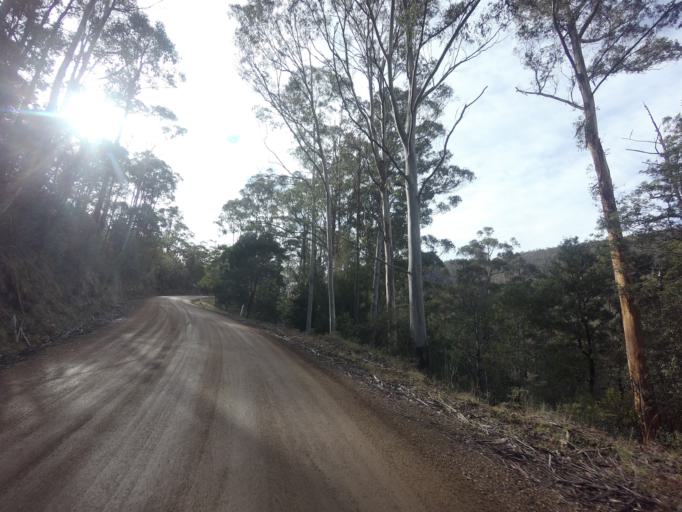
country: AU
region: Tasmania
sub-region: Derwent Valley
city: New Norfolk
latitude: -42.7915
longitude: 146.9405
